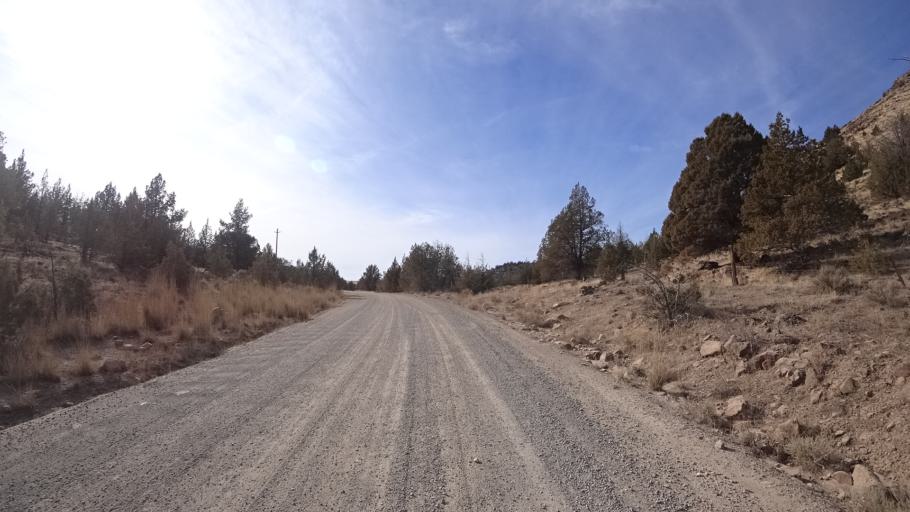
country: US
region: California
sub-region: Siskiyou County
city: Montague
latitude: 41.5835
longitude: -122.4504
